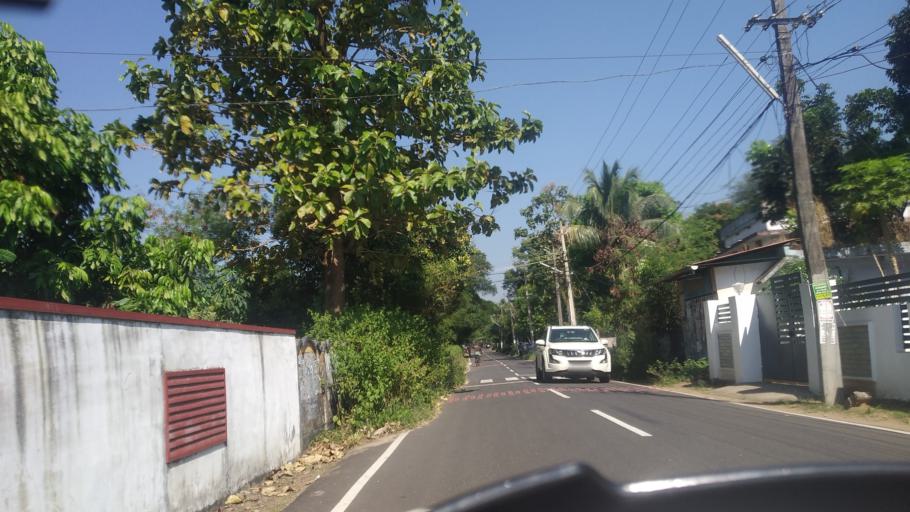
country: IN
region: Kerala
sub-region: Ernakulam
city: Elur
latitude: 10.1169
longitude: 76.2473
